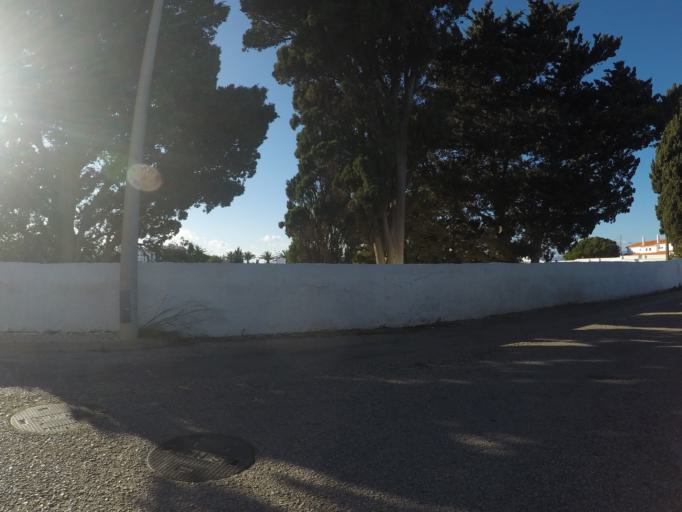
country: PT
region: Faro
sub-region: Lagos
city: Lagos
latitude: 37.0944
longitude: -8.6705
